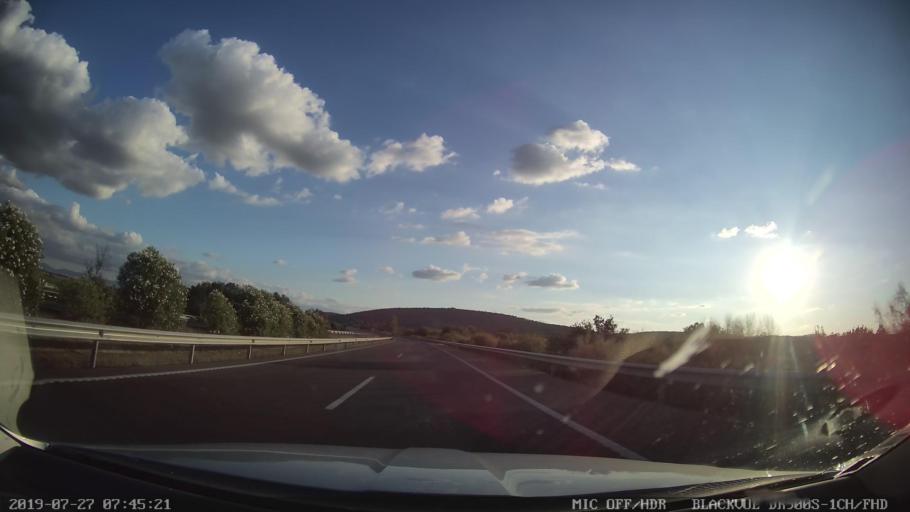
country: ES
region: Extremadura
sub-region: Provincia de Badajoz
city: San Pedro de Merida
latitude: 38.9870
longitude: -6.1351
